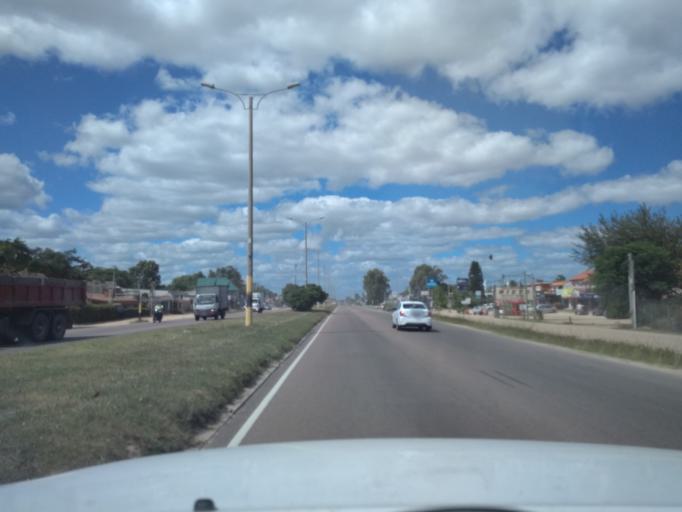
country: UY
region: Canelones
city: Barra de Carrasco
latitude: -34.8381
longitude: -55.9879
